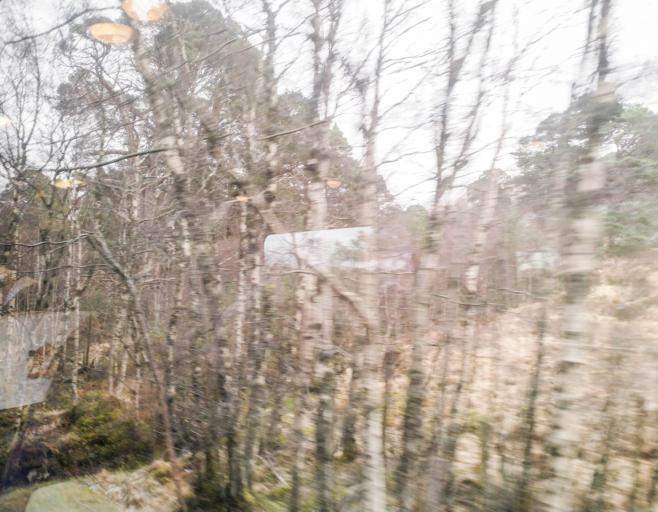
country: GB
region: Scotland
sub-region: Highland
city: Spean Bridge
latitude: 56.5789
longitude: -4.6787
